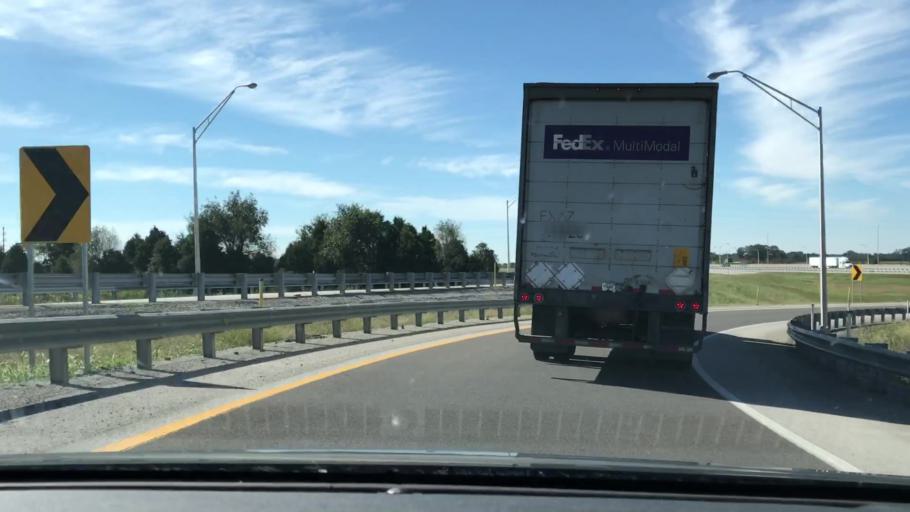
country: US
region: Kentucky
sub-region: Warren County
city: Plano
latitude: 36.9085
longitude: -86.4309
